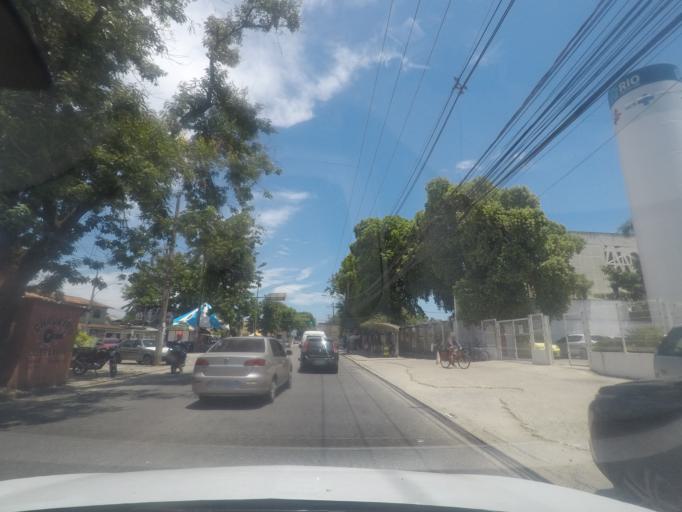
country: BR
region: Rio de Janeiro
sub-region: Itaguai
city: Itaguai
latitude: -22.9383
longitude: -43.6866
